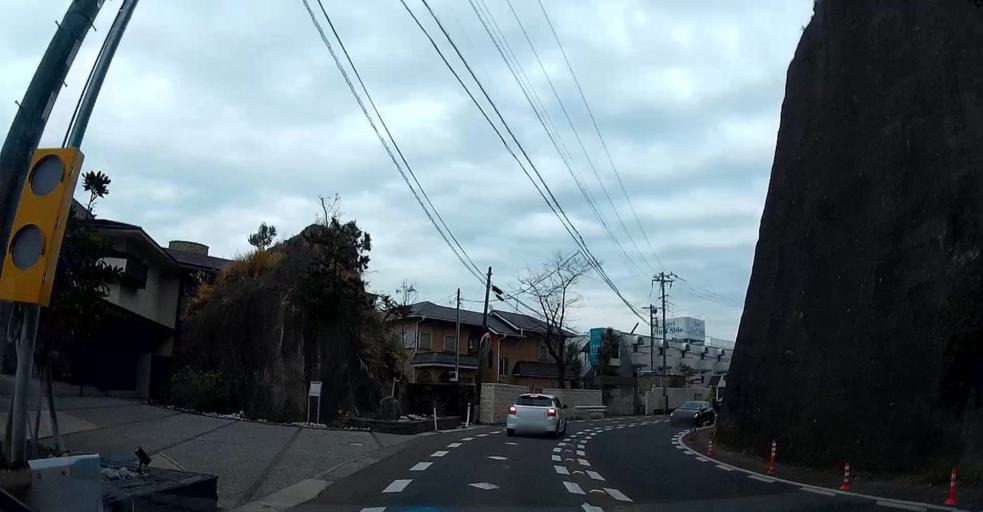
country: JP
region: Kanagawa
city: Miura
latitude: 35.1721
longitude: 139.6584
